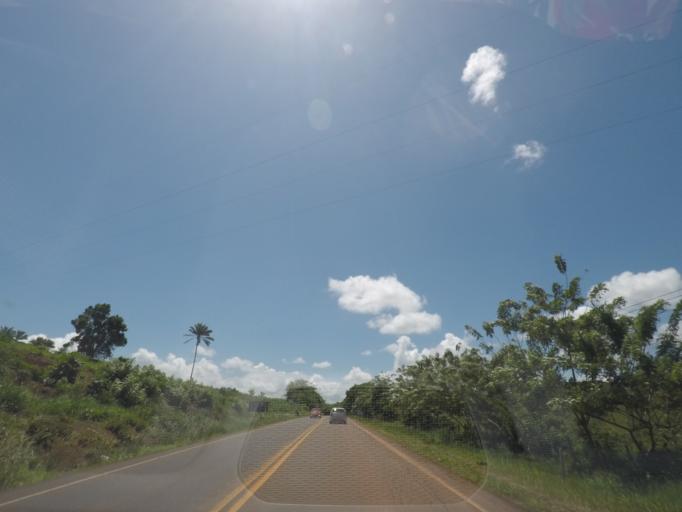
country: BR
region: Bahia
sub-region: Valenca
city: Valenca
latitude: -13.3352
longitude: -39.0600
